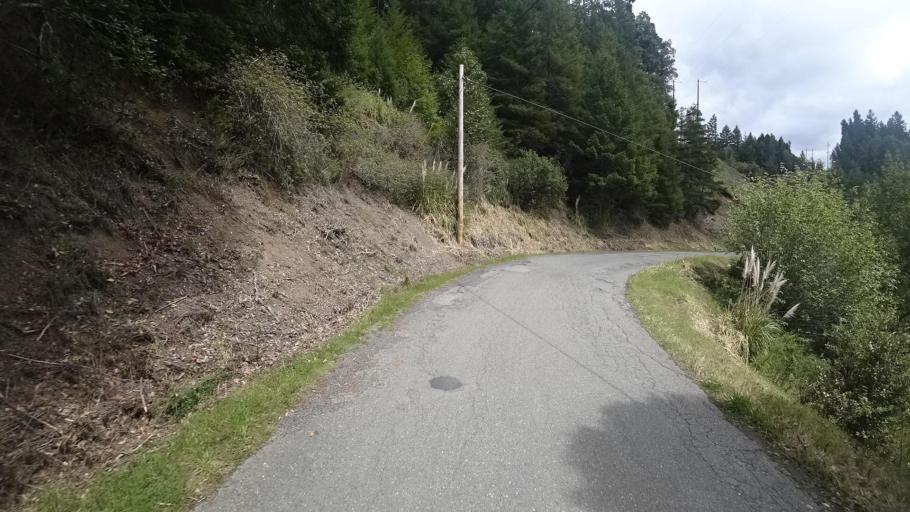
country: US
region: California
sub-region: Humboldt County
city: Blue Lake
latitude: 40.7673
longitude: -123.9304
